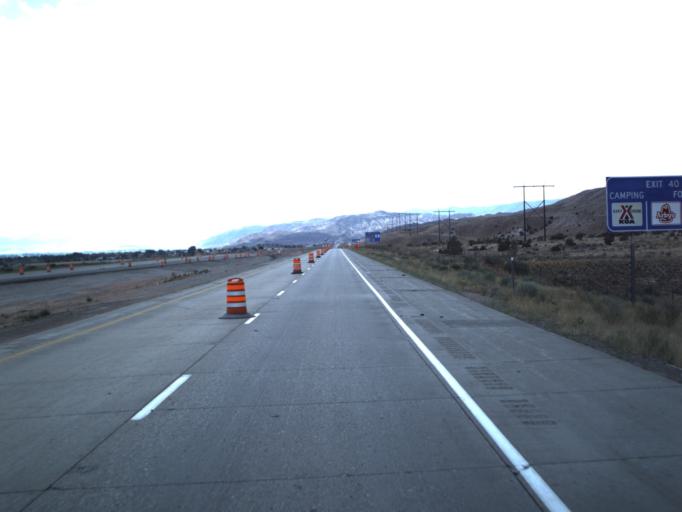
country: US
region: Utah
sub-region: Sevier County
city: Richfield
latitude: 38.8123
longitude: -112.0558
